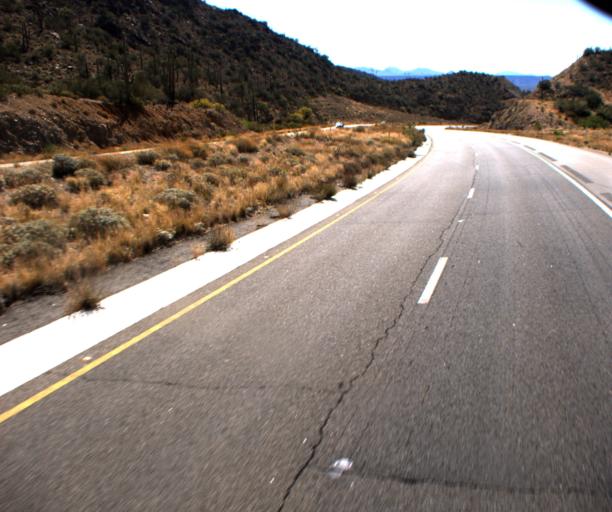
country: US
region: Arizona
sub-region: Yavapai County
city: Bagdad
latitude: 34.4112
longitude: -113.2305
